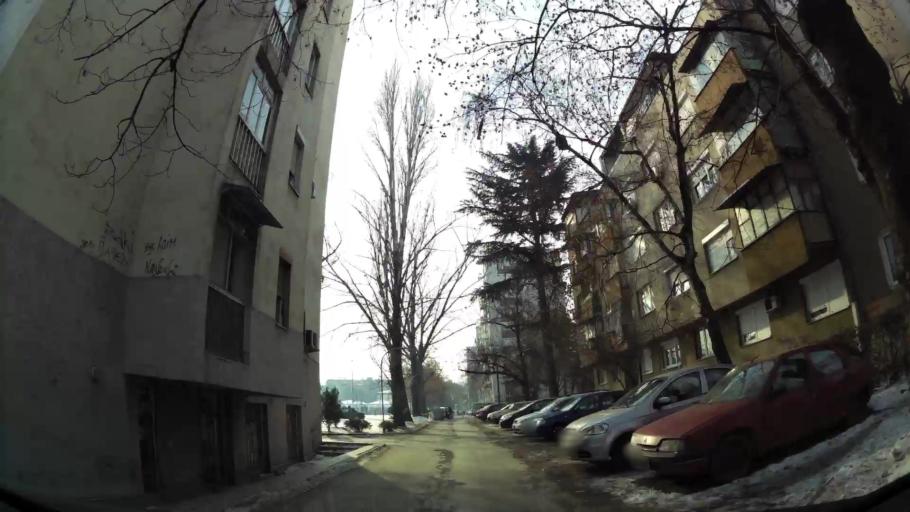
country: MK
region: Cair
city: Cair
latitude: 42.0175
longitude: 21.4327
